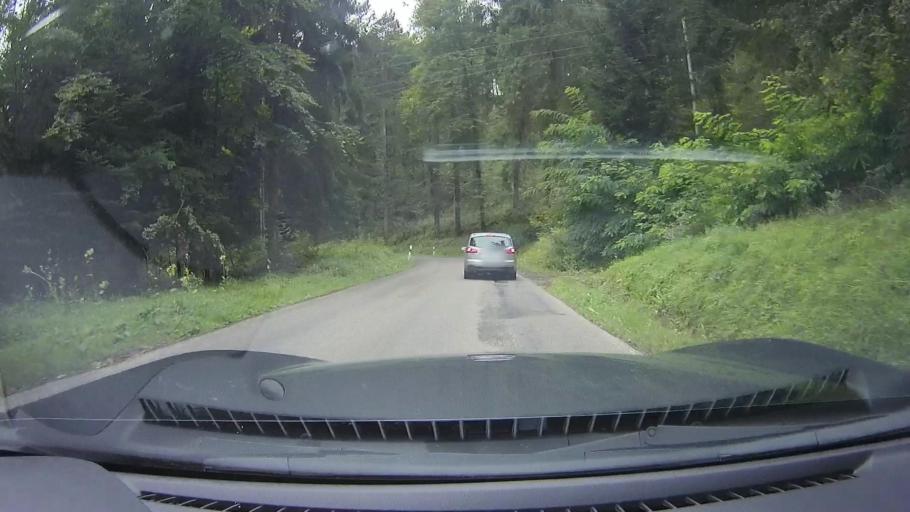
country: DE
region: Baden-Wuerttemberg
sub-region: Regierungsbezirk Stuttgart
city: Murrhardt
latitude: 48.9924
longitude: 9.5743
